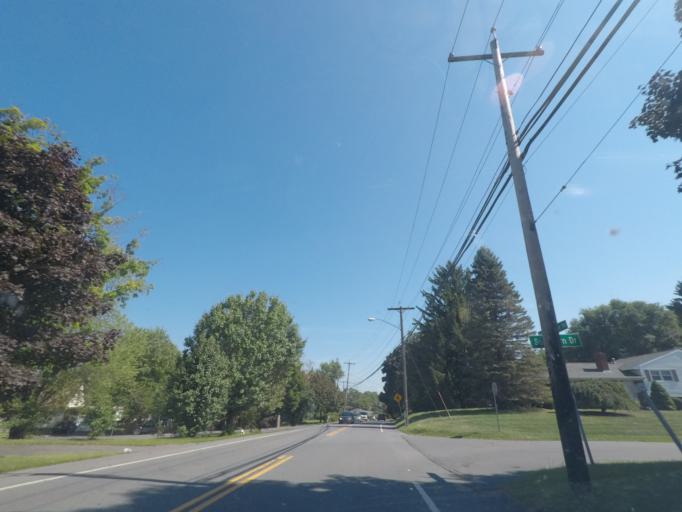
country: US
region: New York
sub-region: Albany County
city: Menands
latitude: 42.7352
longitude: -73.7573
